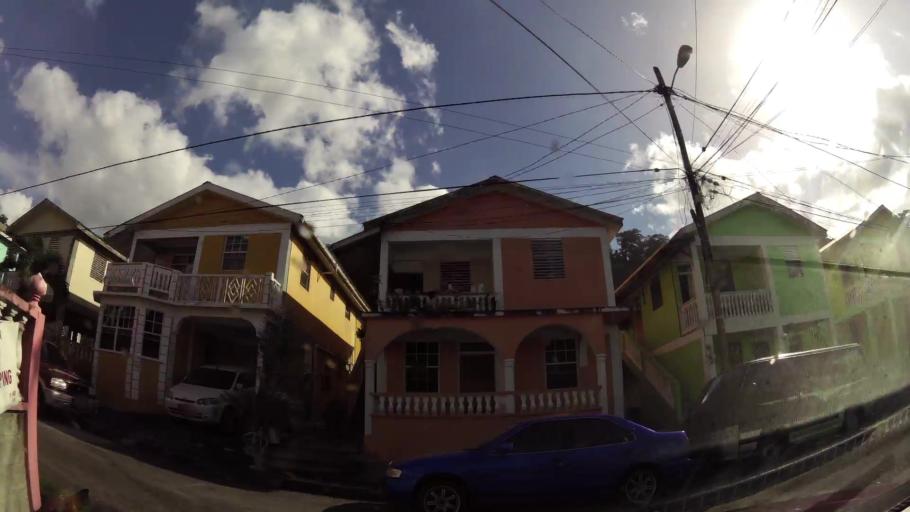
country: DM
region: Saint George
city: Roseau
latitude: 15.3024
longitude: -61.3774
